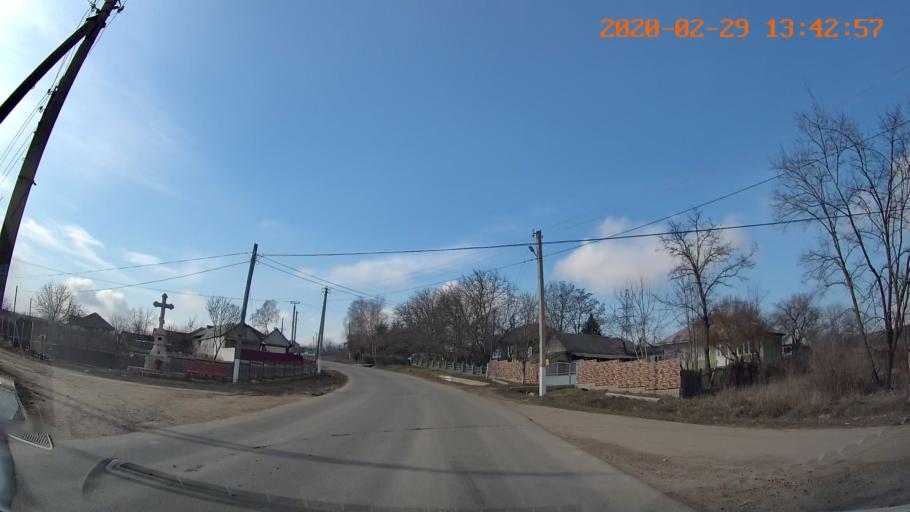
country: MD
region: Floresti
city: Leninskiy
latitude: 47.8410
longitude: 28.5399
